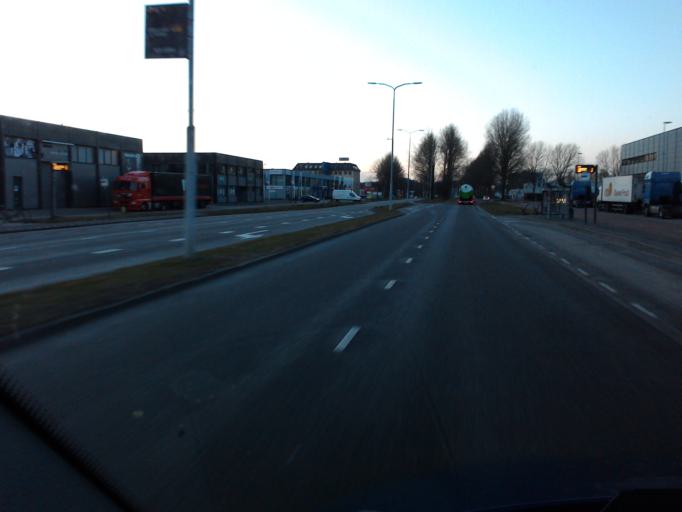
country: NL
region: Utrecht
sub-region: Stichtse Vecht
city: Maarssen
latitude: 52.1177
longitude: 5.0463
